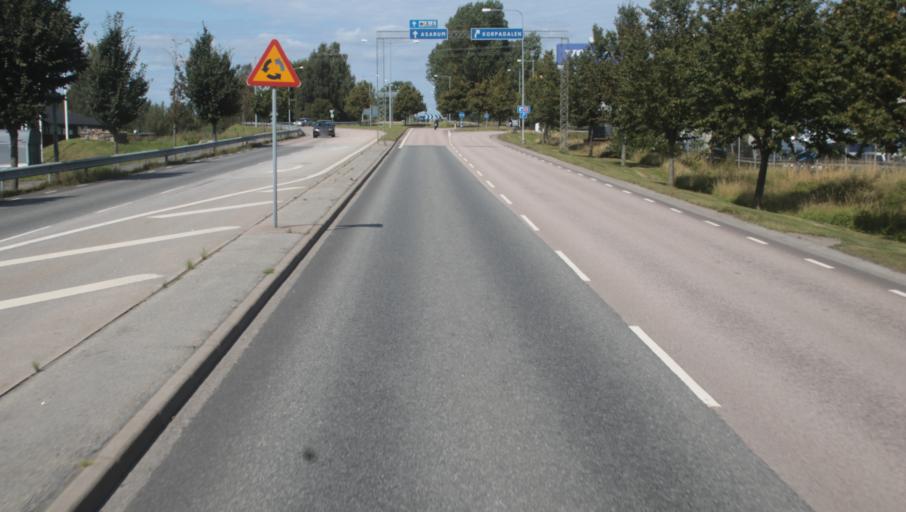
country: SE
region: Blekinge
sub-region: Karlshamns Kommun
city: Karlshamn
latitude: 56.1927
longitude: 14.8433
